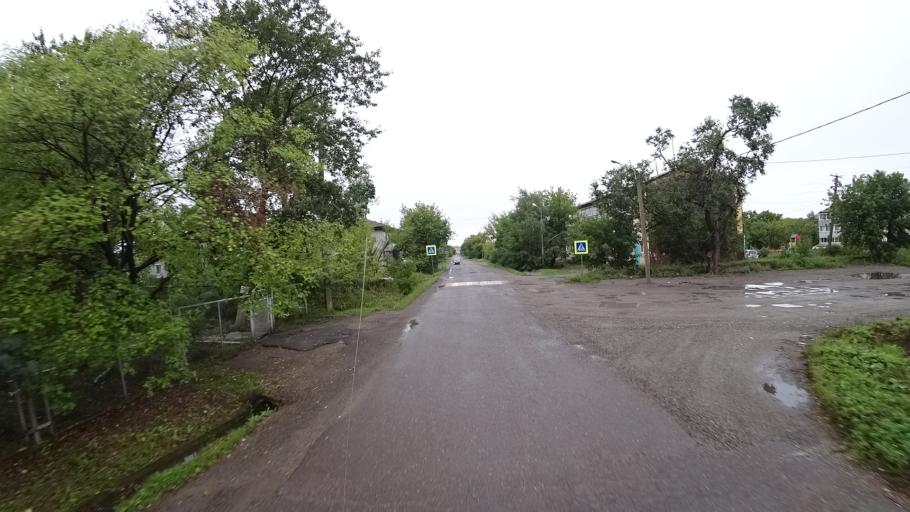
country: RU
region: Primorskiy
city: Monastyrishche
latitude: 44.2031
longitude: 132.4584
